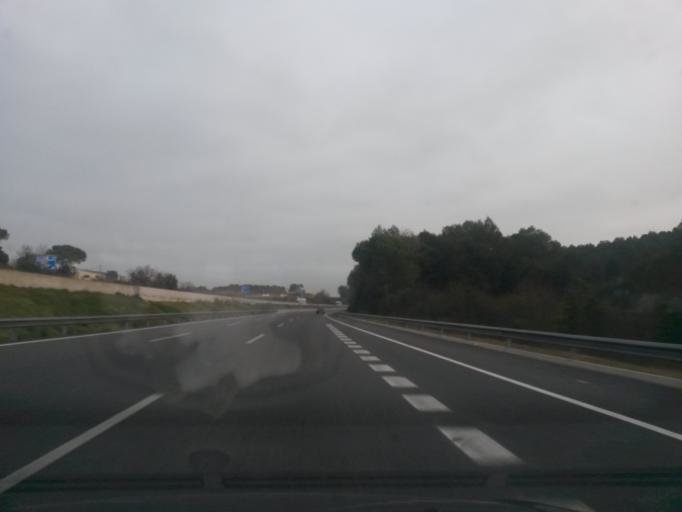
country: ES
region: Catalonia
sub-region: Provincia de Girona
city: Cervia de Ter
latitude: 42.0843
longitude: 2.8902
